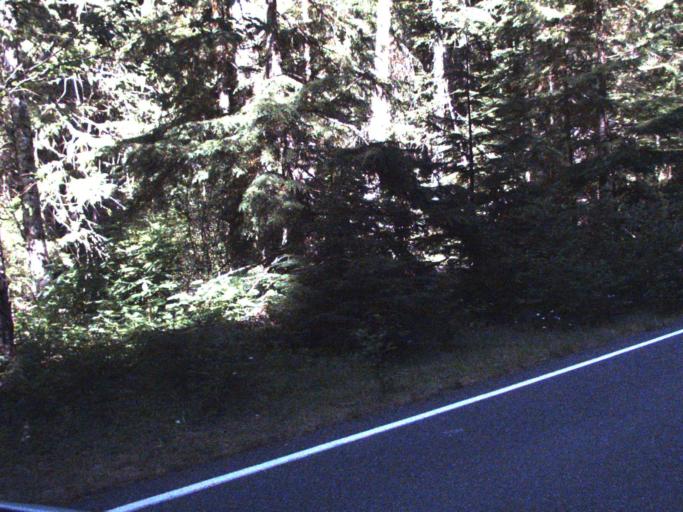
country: US
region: Washington
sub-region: King County
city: Enumclaw
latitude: 46.9694
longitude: -121.5329
